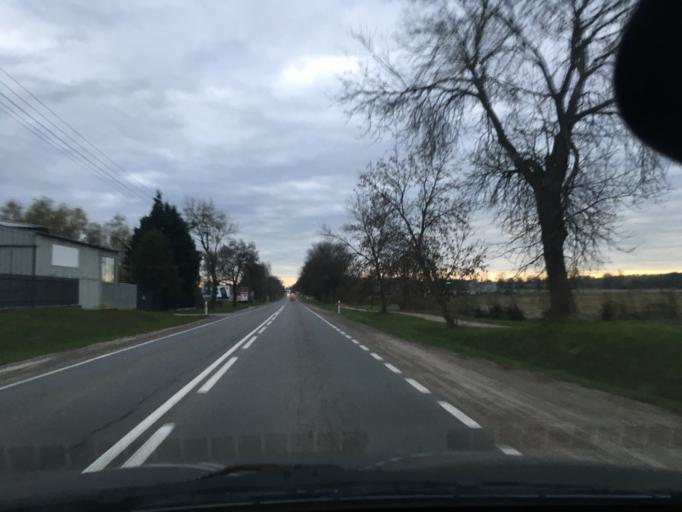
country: PL
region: Masovian Voivodeship
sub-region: Powiat piaseczynski
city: Lesznowola
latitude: 52.0947
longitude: 20.9261
